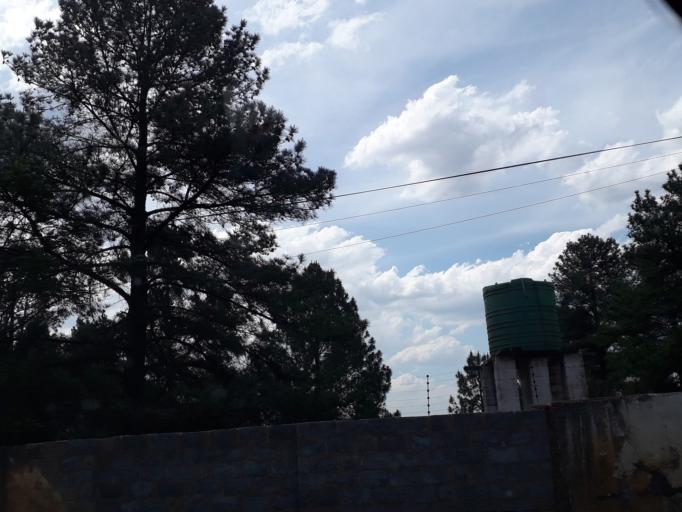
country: ZA
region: Gauteng
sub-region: City of Johannesburg Metropolitan Municipality
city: Roodepoort
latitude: -26.0909
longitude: 27.9054
